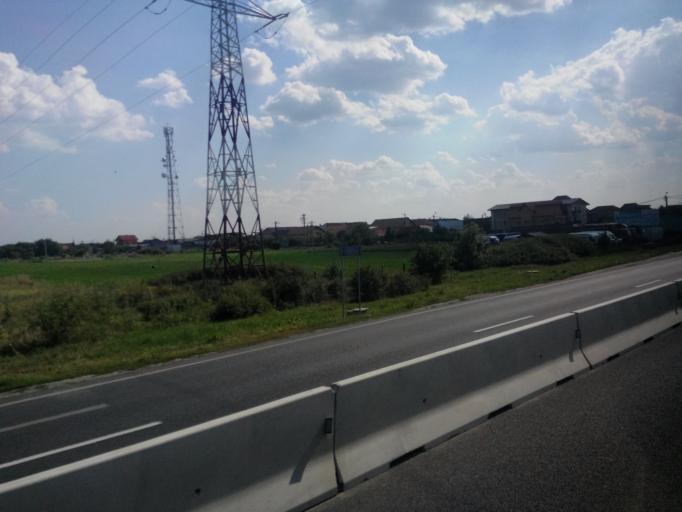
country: RO
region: Timis
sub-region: Comuna Ghiroda
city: Ghiroda
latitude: 45.7766
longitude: 21.3084
